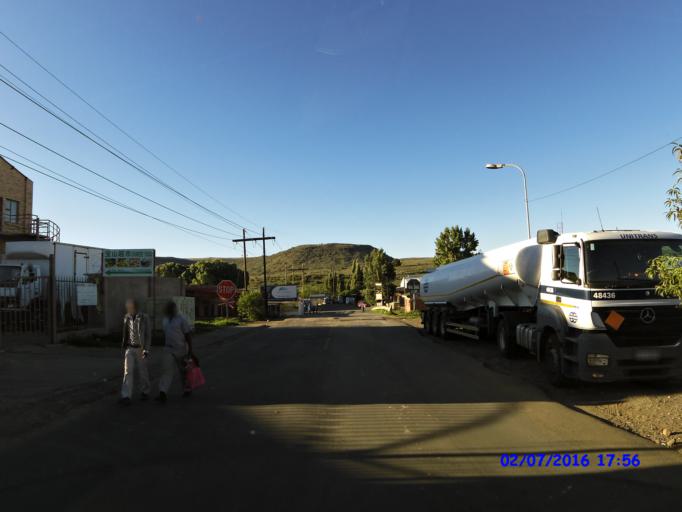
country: LS
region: Maseru
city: Maseru
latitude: -29.2975
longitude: 27.4733
